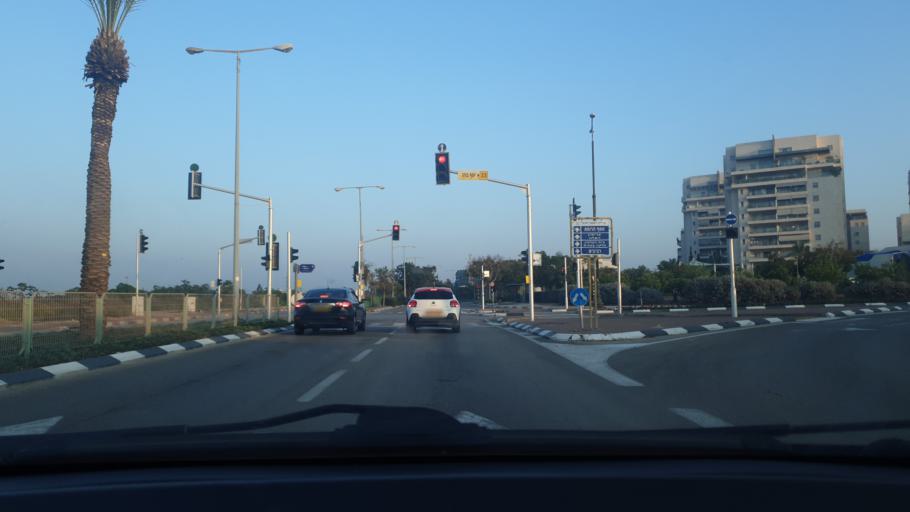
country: IL
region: Central District
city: Bet Dagan
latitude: 31.9717
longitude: 34.8225
